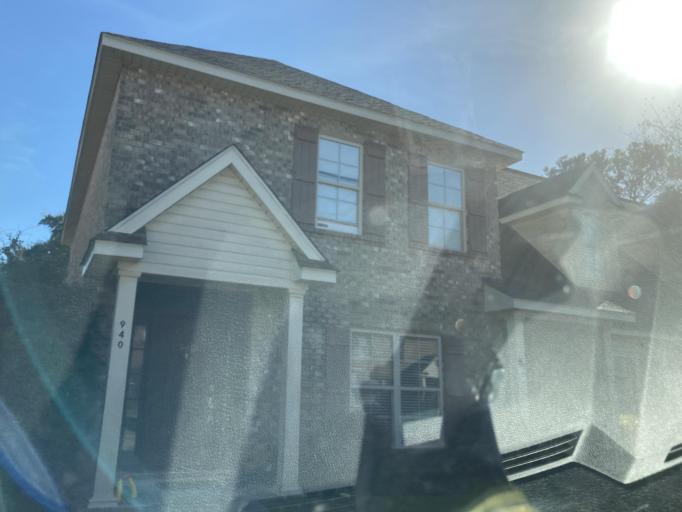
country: US
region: Mississippi
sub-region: Harrison County
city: West Gulfport
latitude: 30.4057
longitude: -89.0022
